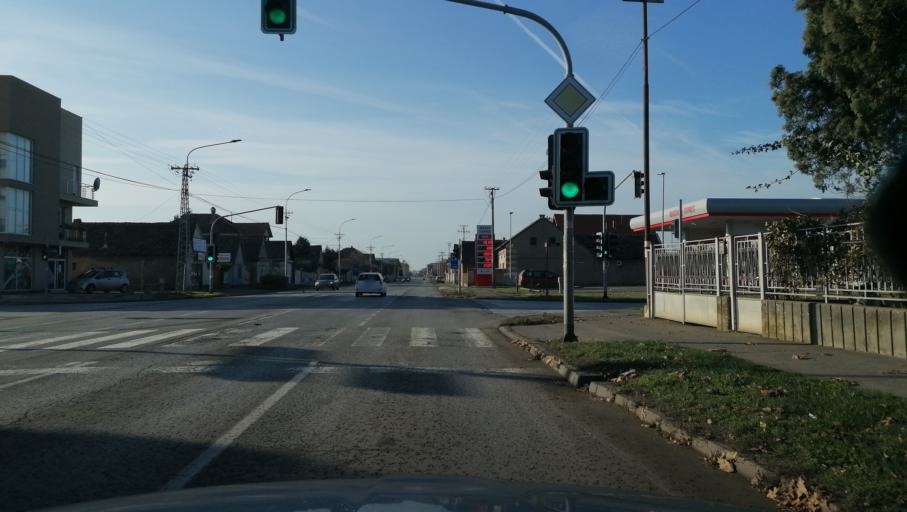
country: RS
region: Autonomna Pokrajina Vojvodina
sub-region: Sremski Okrug
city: Sremska Mitrovica
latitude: 44.9710
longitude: 19.6267
